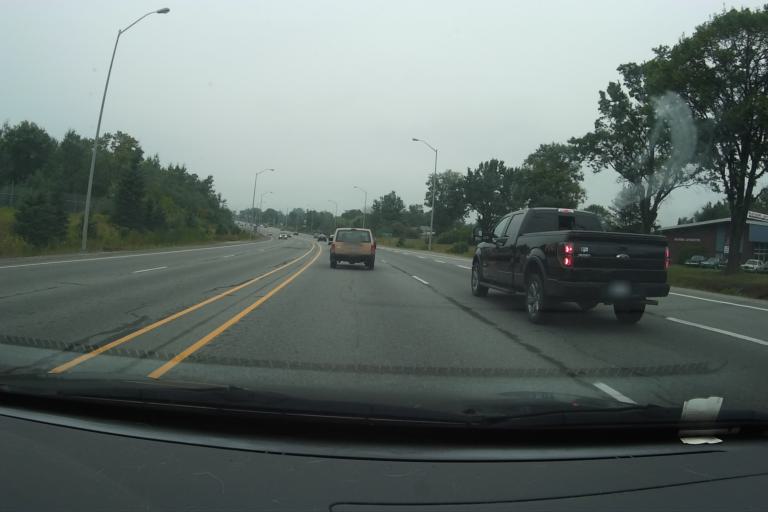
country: CA
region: Ontario
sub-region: Nipissing District
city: North Bay
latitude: 46.3270
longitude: -79.4524
